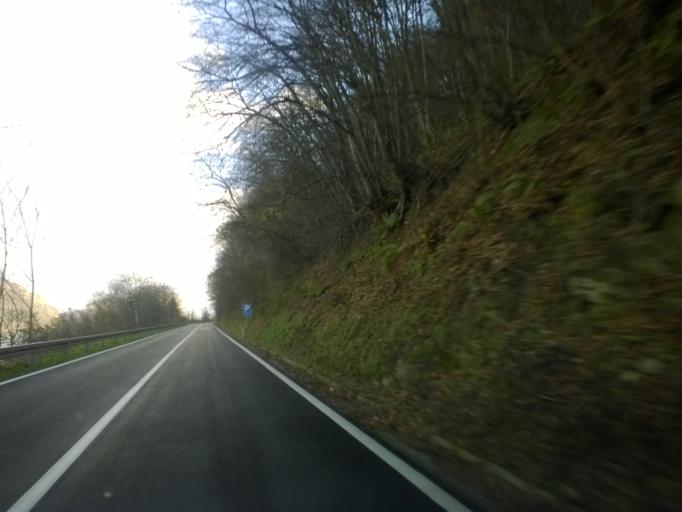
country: RS
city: Radenka
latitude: 44.6554
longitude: 21.7905
